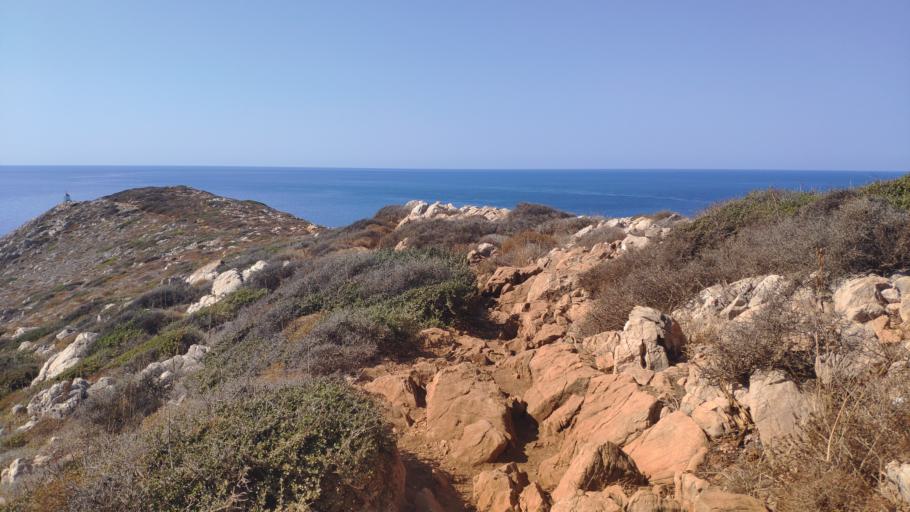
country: GR
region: Peloponnese
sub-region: Nomos Lakonias
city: Gytheio
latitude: 36.3900
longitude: 22.4827
